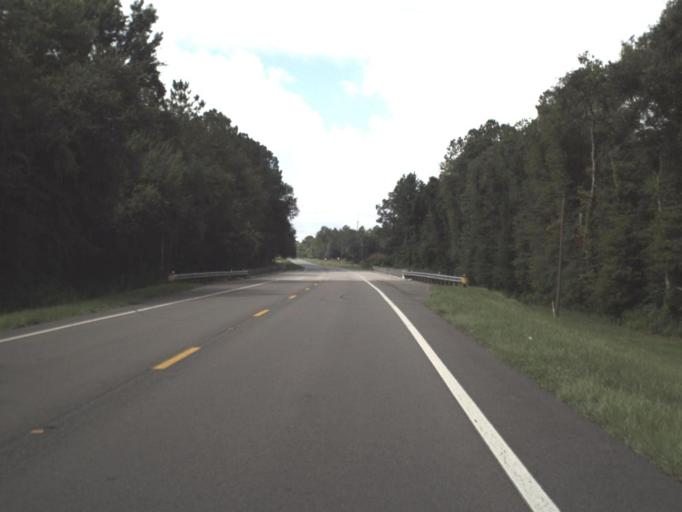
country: US
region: Florida
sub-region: Columbia County
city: Five Points
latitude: 30.2667
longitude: -82.6358
